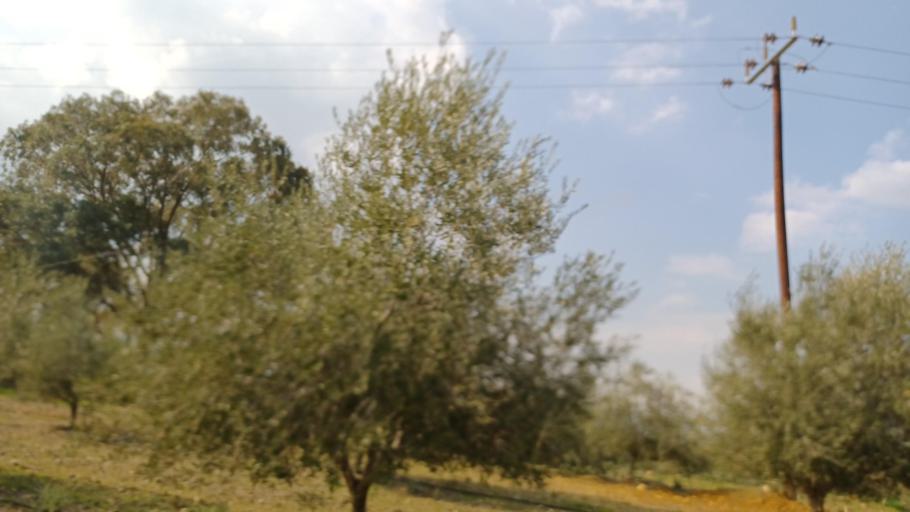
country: CY
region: Pafos
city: Polis
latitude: 35.0494
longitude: 32.4597
